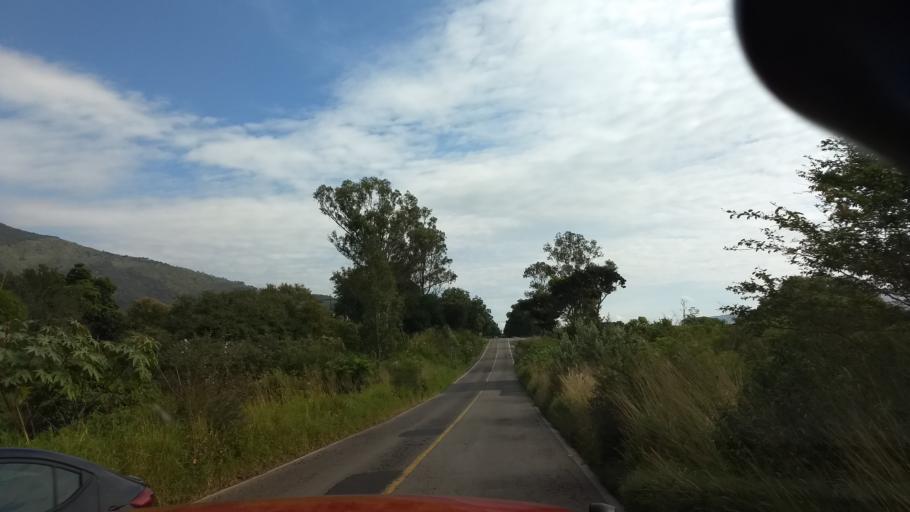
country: MX
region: Jalisco
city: Tuxpan
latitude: 19.5388
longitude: -103.4095
